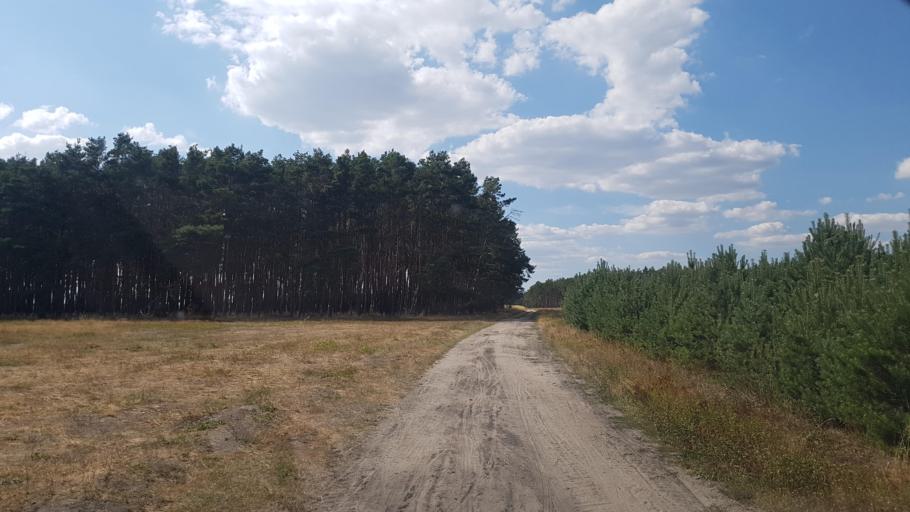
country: DE
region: Saxony-Anhalt
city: Elster
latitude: 51.8434
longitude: 12.8058
